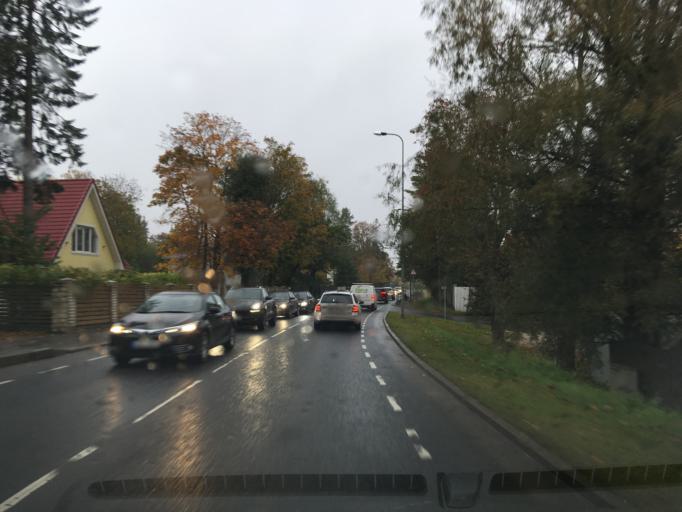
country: EE
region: Harju
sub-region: Tallinna linn
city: Kose
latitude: 59.4568
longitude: 24.8649
